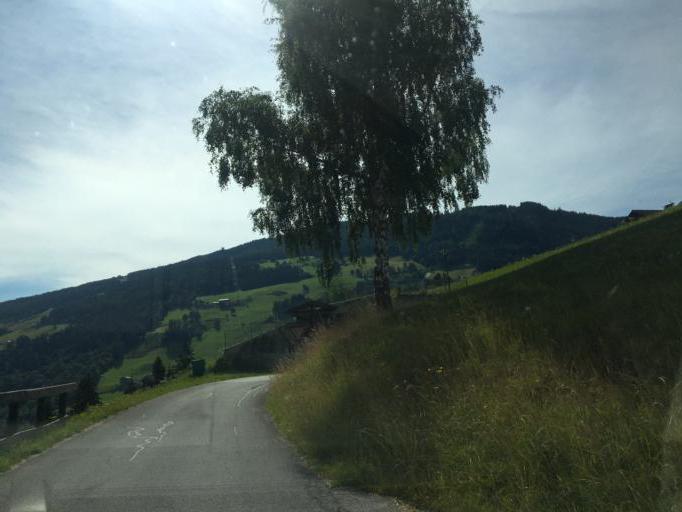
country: AT
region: Styria
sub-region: Politischer Bezirk Liezen
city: Schladming
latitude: 47.3869
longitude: 13.6743
